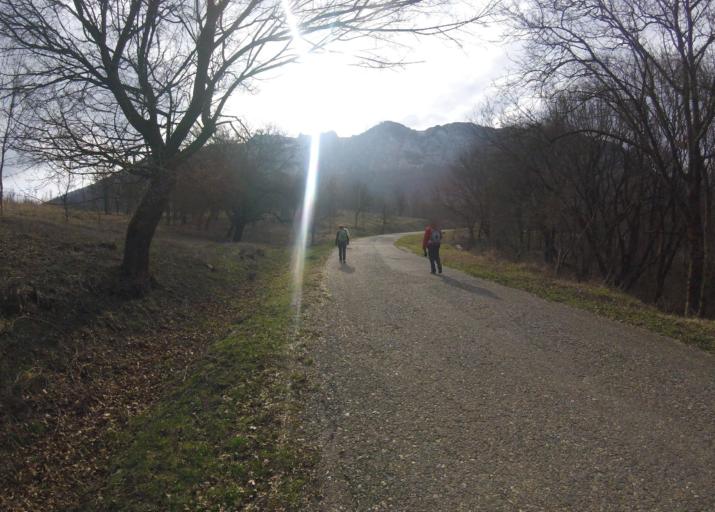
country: HU
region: Heves
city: Belapatfalva
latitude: 48.0509
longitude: 20.3654
